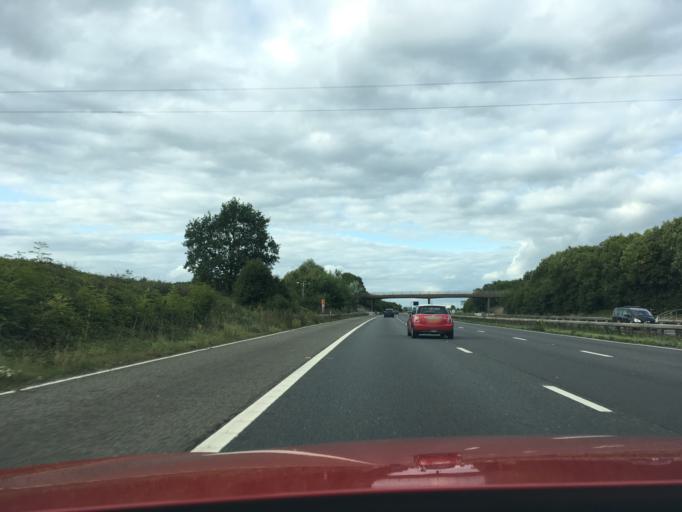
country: GB
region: England
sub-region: Gloucestershire
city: Stonehouse
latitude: 51.7766
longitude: -2.3096
